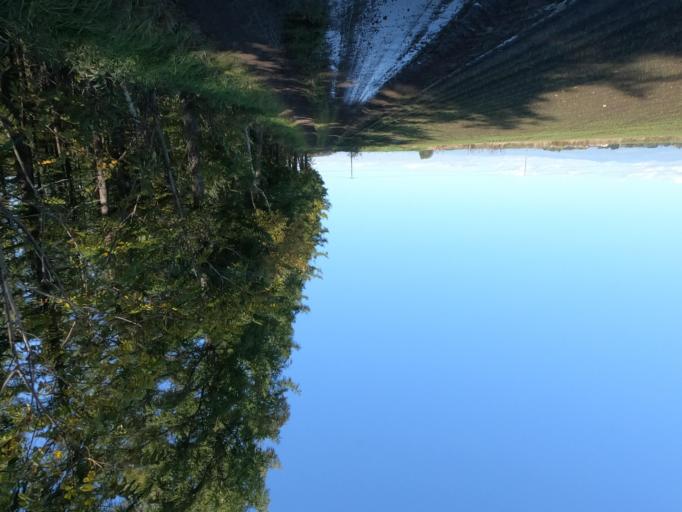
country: JP
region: Hokkaido
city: Otofuke
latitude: 43.0161
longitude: 143.2698
